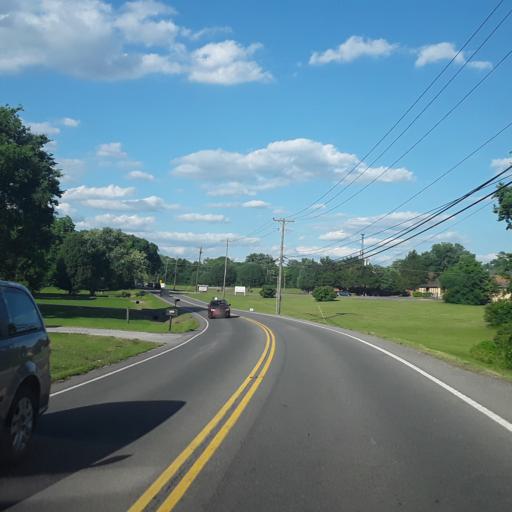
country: US
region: Tennessee
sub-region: Wilson County
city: Green Hill
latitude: 36.1715
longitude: -86.5893
